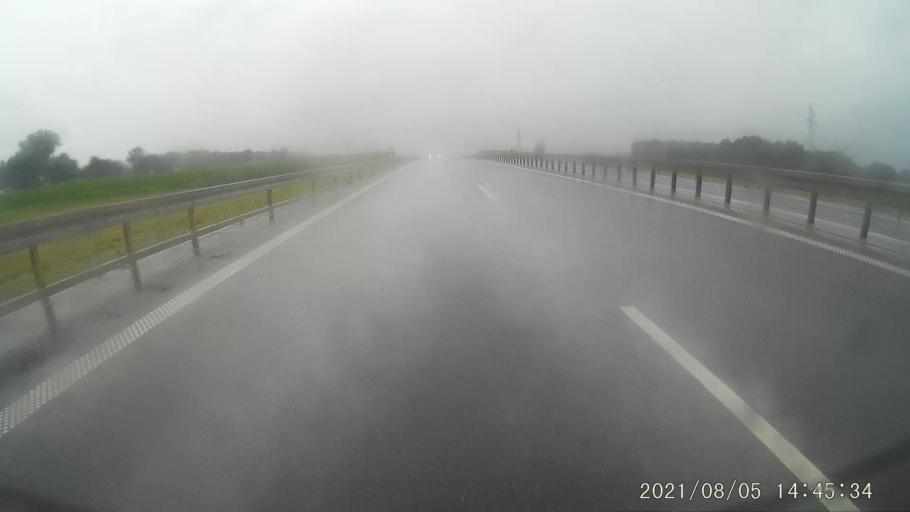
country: PL
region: Opole Voivodeship
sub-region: Powiat nyski
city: Nysa
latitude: 50.4995
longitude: 17.3561
